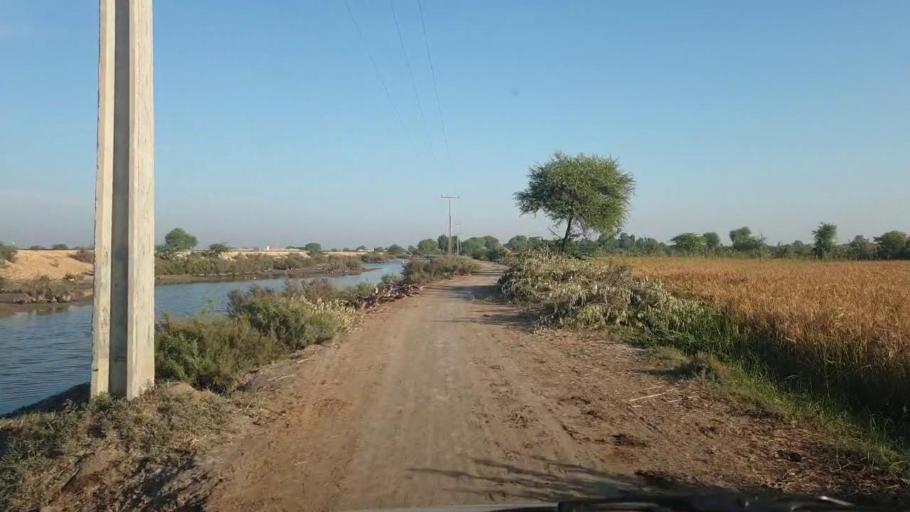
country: PK
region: Sindh
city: Talhar
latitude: 24.7961
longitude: 68.8170
